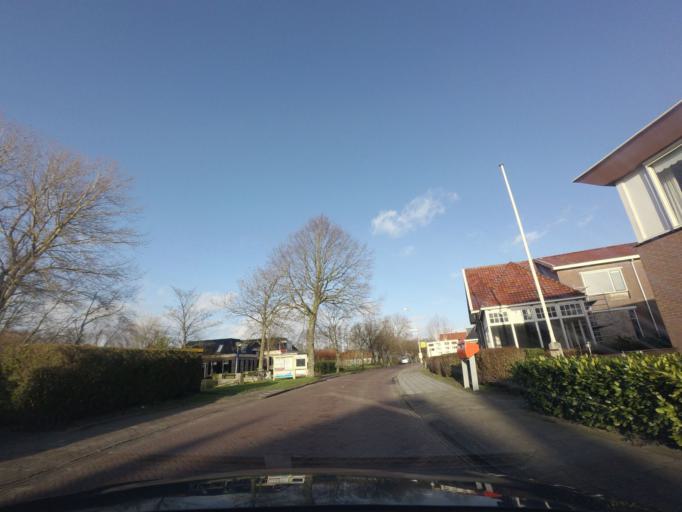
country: NL
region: North Holland
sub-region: Gemeente Opmeer
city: Opmeer
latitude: 52.7343
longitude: 4.8877
